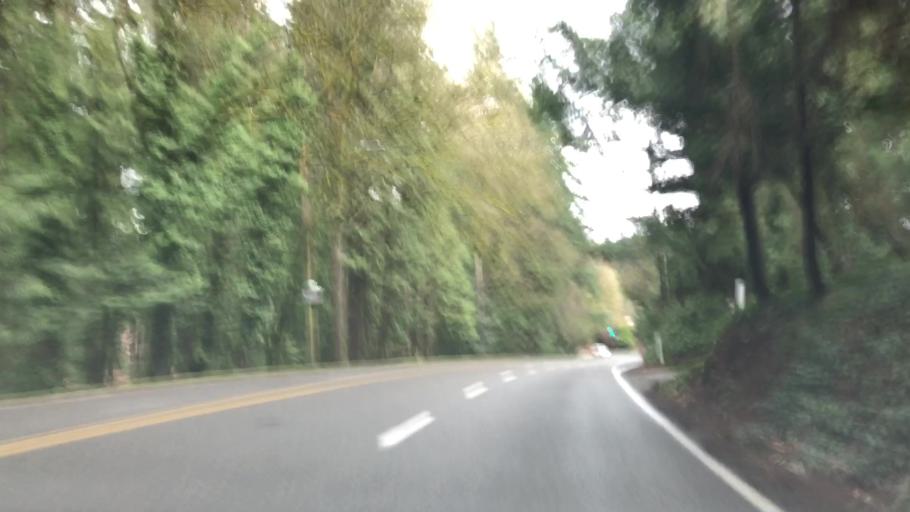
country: US
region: Oregon
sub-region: Washington County
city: West Slope
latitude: 45.4966
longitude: -122.7414
